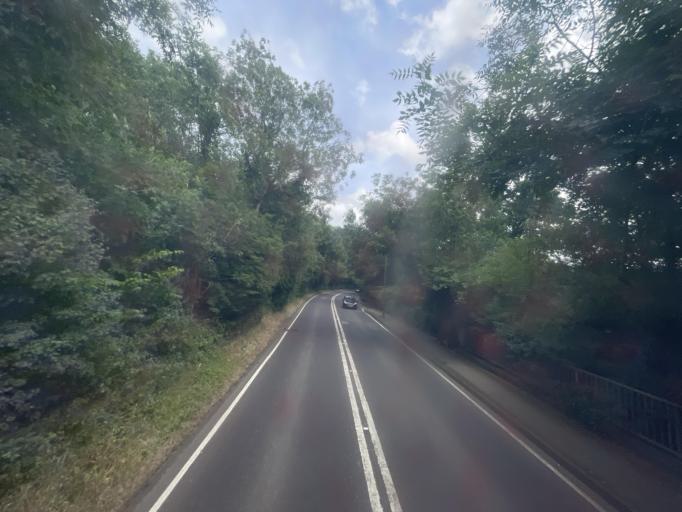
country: GB
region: England
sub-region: Kent
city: Biggin Hill
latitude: 51.3510
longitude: 0.0336
